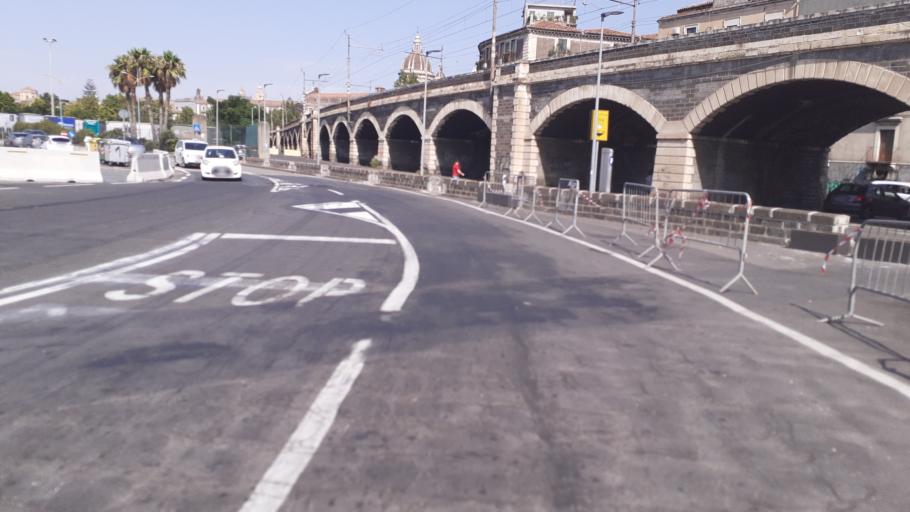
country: IT
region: Sicily
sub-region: Catania
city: Catania
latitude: 37.5008
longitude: 15.0921
